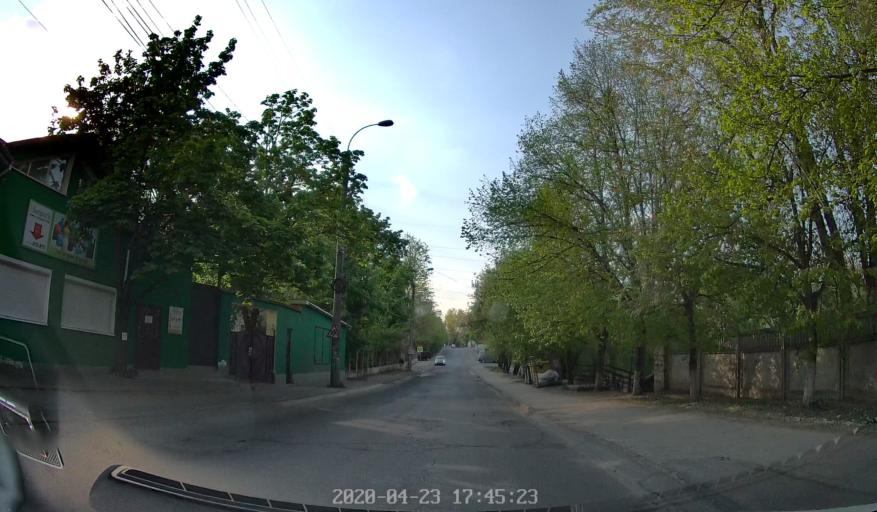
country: MD
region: Chisinau
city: Chisinau
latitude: 46.9954
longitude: 28.8255
